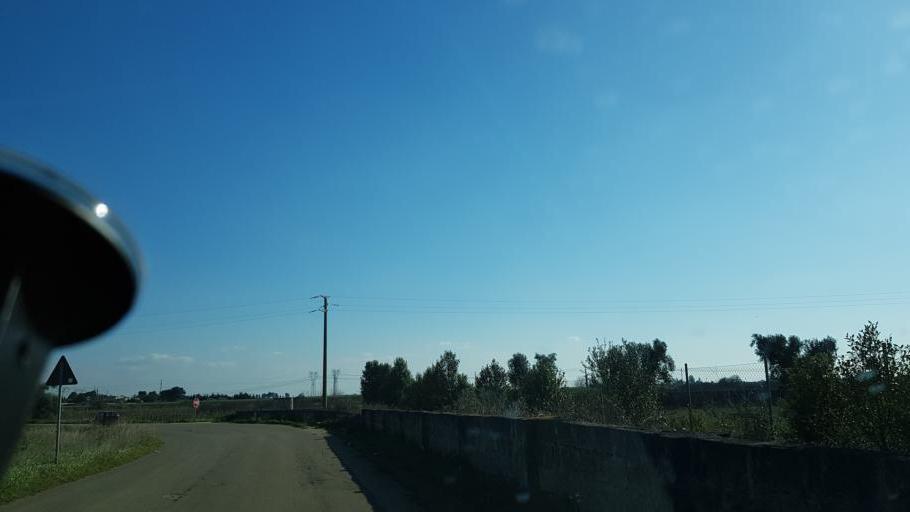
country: IT
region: Apulia
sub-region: Provincia di Brindisi
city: Brindisi
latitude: 40.6087
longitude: 17.8755
